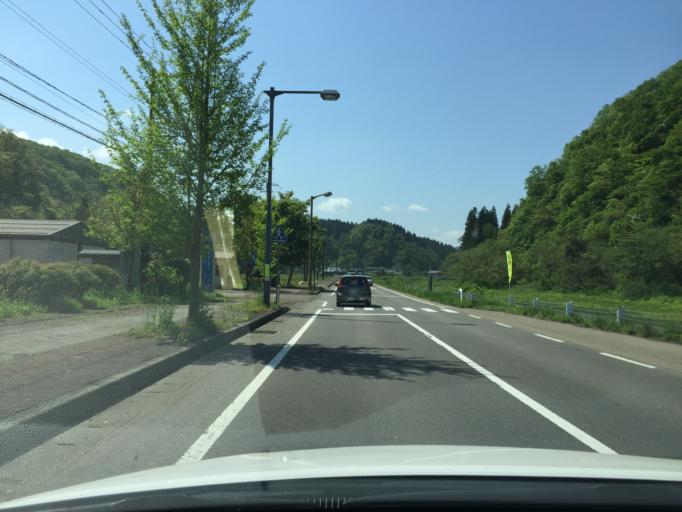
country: JP
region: Niigata
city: Kamo
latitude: 37.6235
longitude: 139.1041
